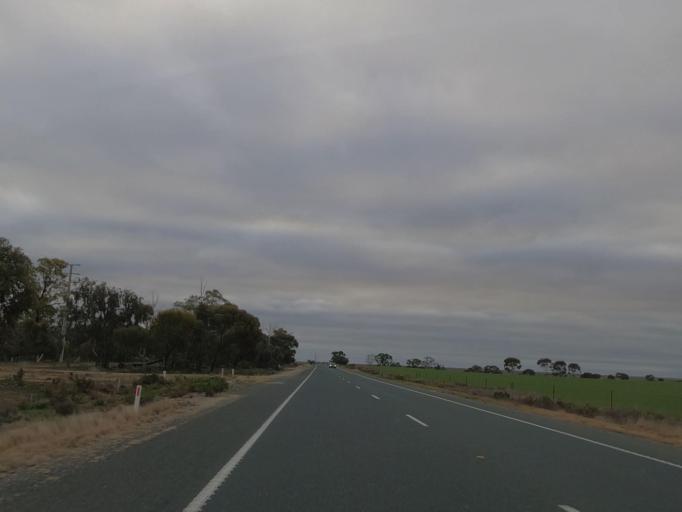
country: AU
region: Victoria
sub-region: Swan Hill
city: Swan Hill
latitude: -35.5584
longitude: 143.7794
